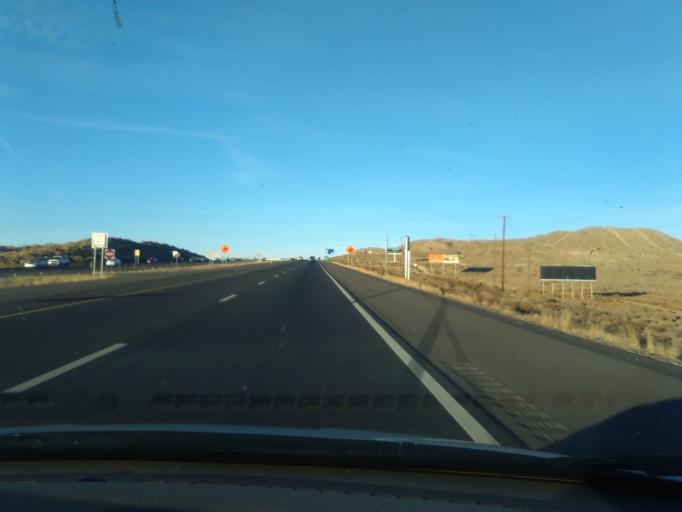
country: US
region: New Mexico
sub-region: Bernalillo County
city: South Valley
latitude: 35.0064
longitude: -106.6430
